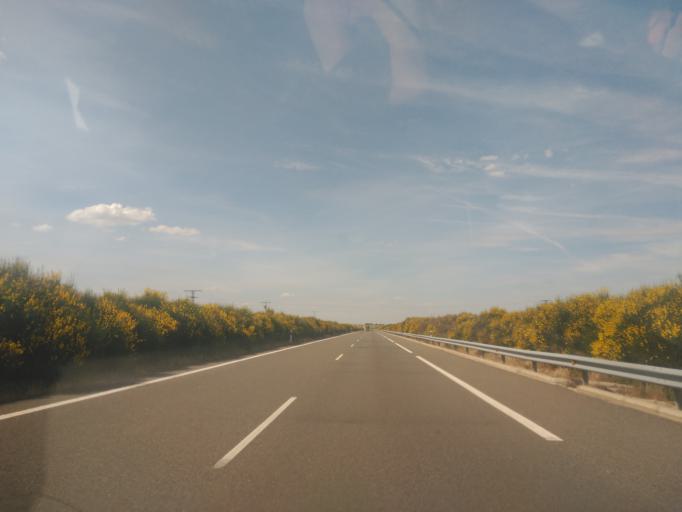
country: ES
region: Castille and Leon
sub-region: Provincia de Salamanca
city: Mozarbez
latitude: 40.8313
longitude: -5.6361
